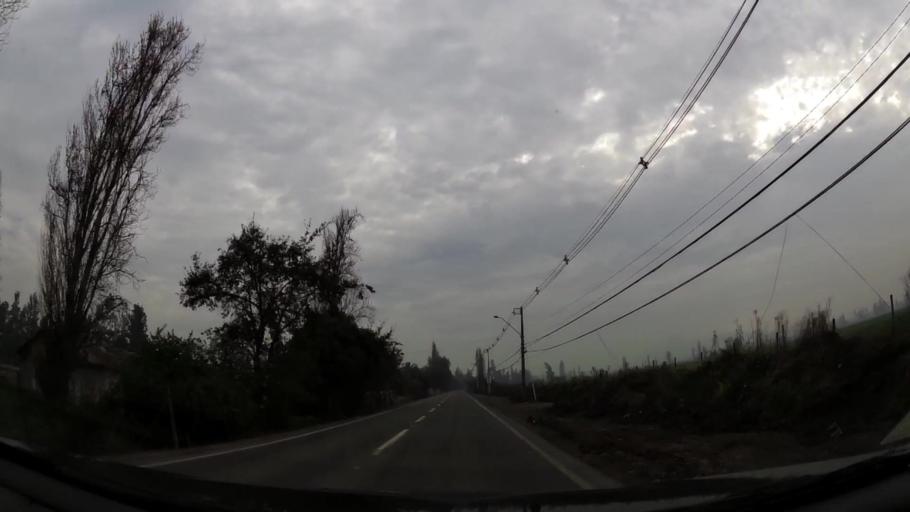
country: CL
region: Santiago Metropolitan
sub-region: Provincia de Chacabuco
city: Chicureo Abajo
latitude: -33.2529
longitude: -70.7632
